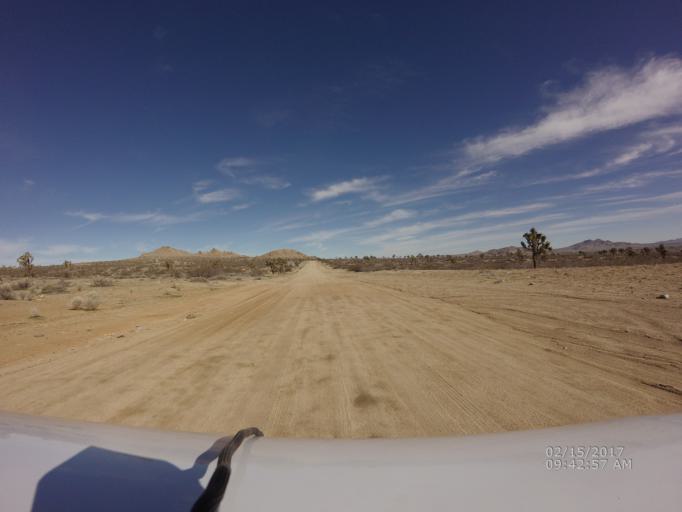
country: US
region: California
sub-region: Los Angeles County
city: Lake Los Angeles
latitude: 34.6174
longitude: -117.8899
